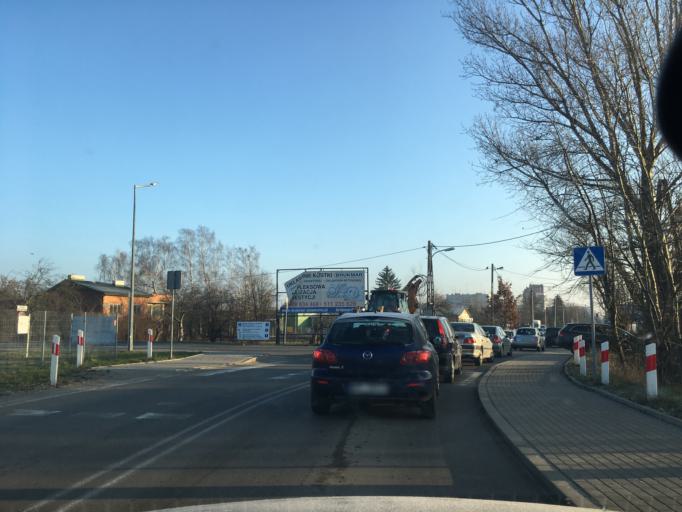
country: PL
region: Masovian Voivodeship
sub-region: Powiat piaseczynski
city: Piaseczno
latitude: 52.0739
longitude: 21.0098
